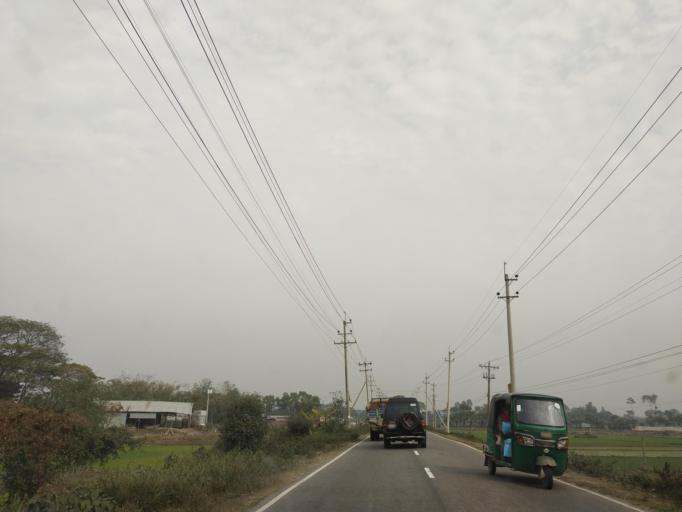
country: BD
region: Dhaka
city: Narsingdi
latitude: 23.9923
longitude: 90.7366
